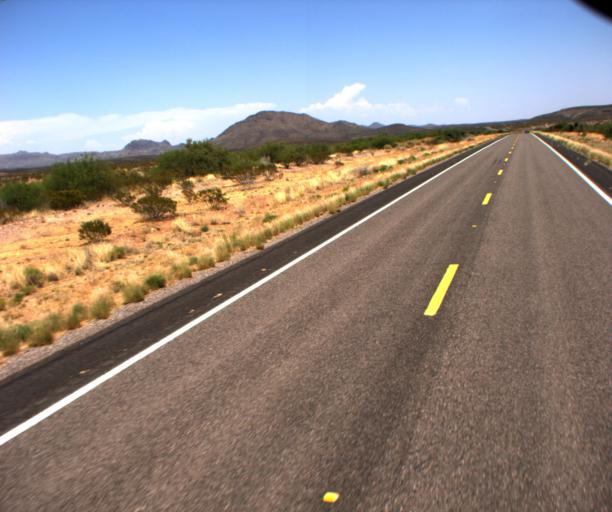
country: US
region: Arizona
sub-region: Graham County
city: Swift Trail Junction
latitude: 32.7572
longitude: -109.4286
